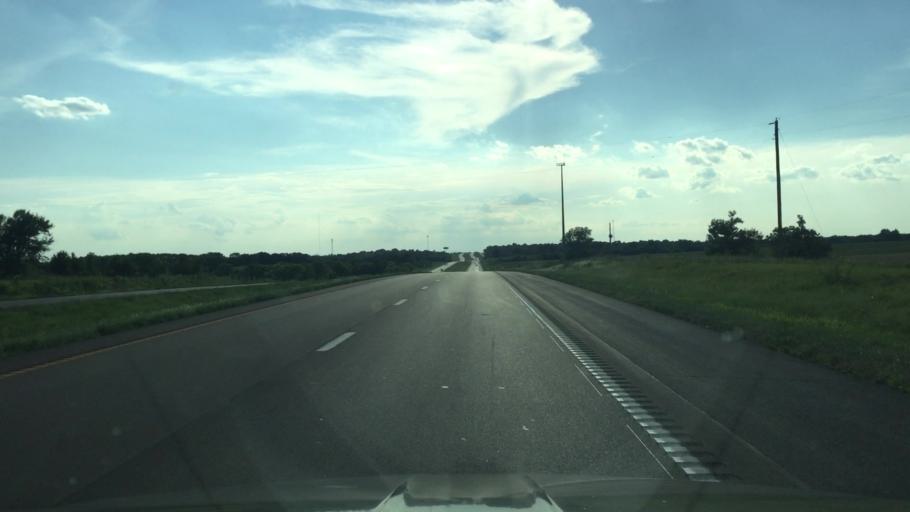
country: US
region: Missouri
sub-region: Pettis County
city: La Monte
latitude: 38.7622
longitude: -93.3942
